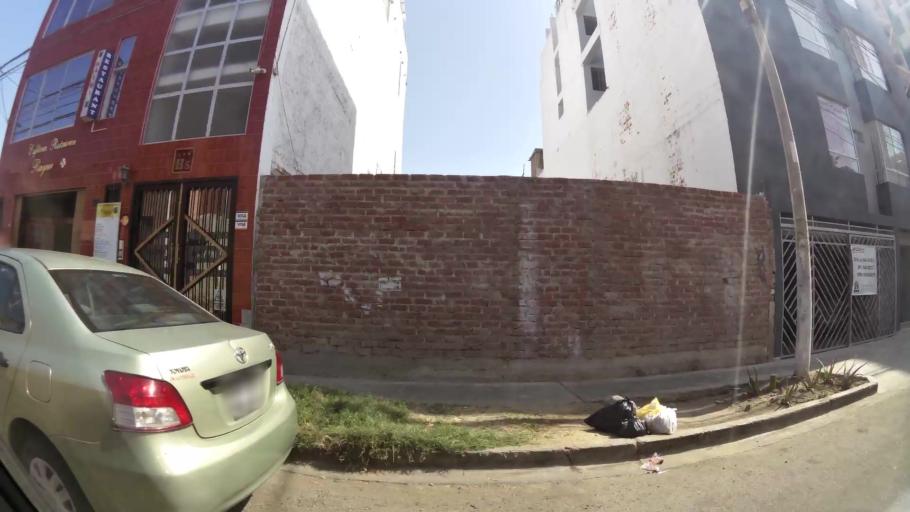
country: PE
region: La Libertad
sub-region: Provincia de Trujillo
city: Trujillo
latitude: -8.1234
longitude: -79.0426
